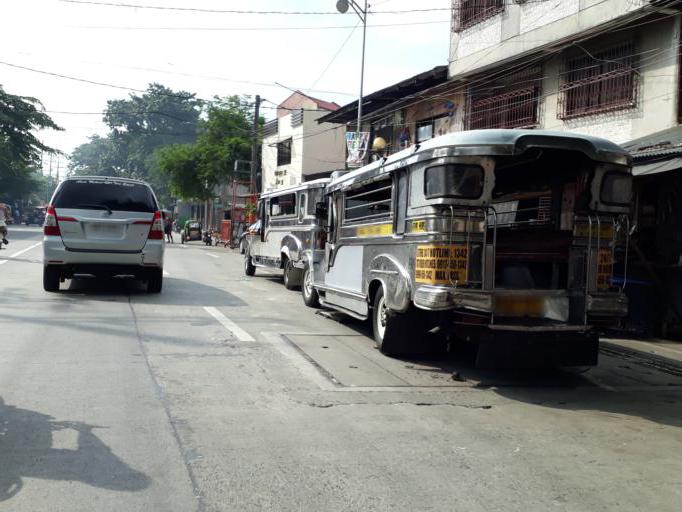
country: PH
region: Metro Manila
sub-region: City of Manila
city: Manila
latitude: 14.6263
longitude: 120.9862
